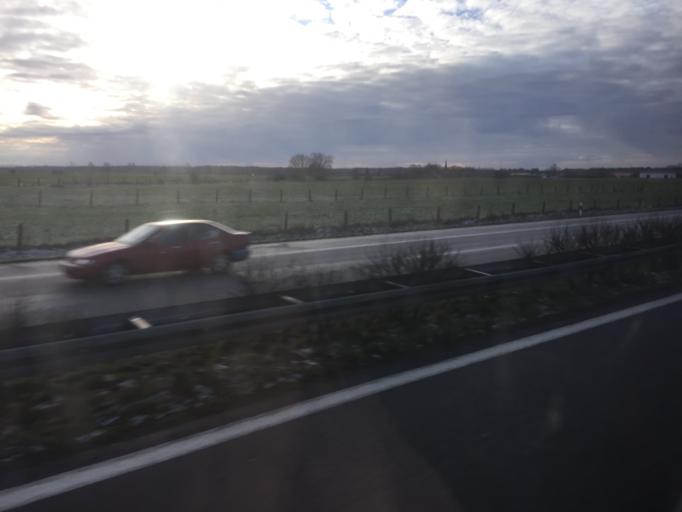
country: DE
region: Mecklenburg-Vorpommern
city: Spornitz
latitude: 53.3687
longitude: 11.6806
